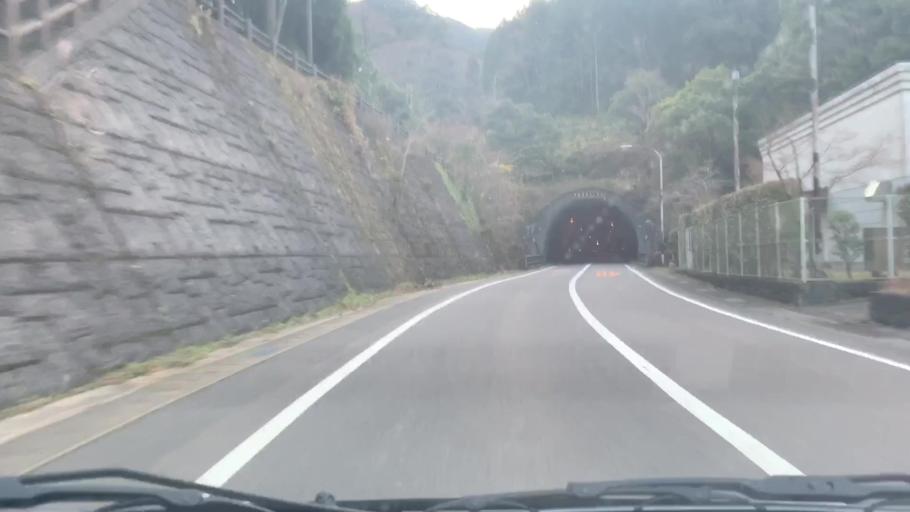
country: JP
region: Saga Prefecture
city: Kashima
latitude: 32.9985
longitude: 130.0621
